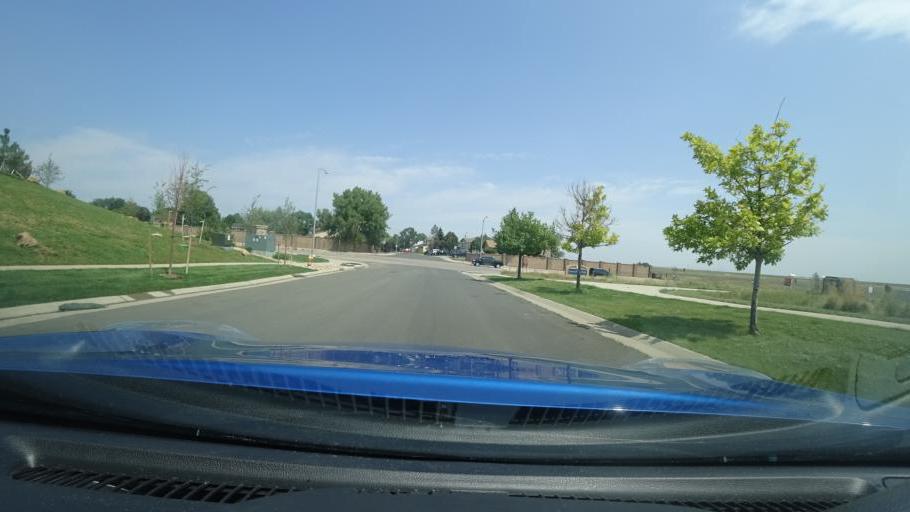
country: US
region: Colorado
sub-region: Adams County
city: Aurora
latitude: 39.6815
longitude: -104.7566
